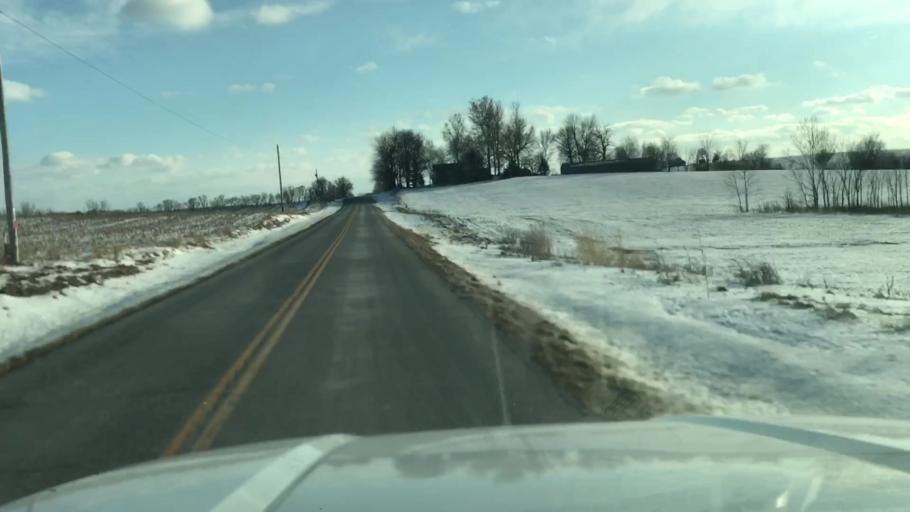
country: US
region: Missouri
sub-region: Holt County
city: Oregon
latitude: 40.0523
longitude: -94.9750
